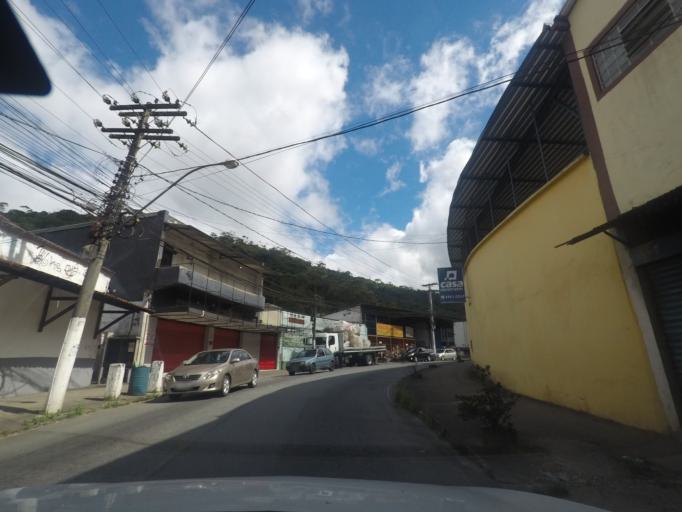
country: BR
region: Rio de Janeiro
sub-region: Teresopolis
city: Teresopolis
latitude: -22.4021
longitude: -42.9641
